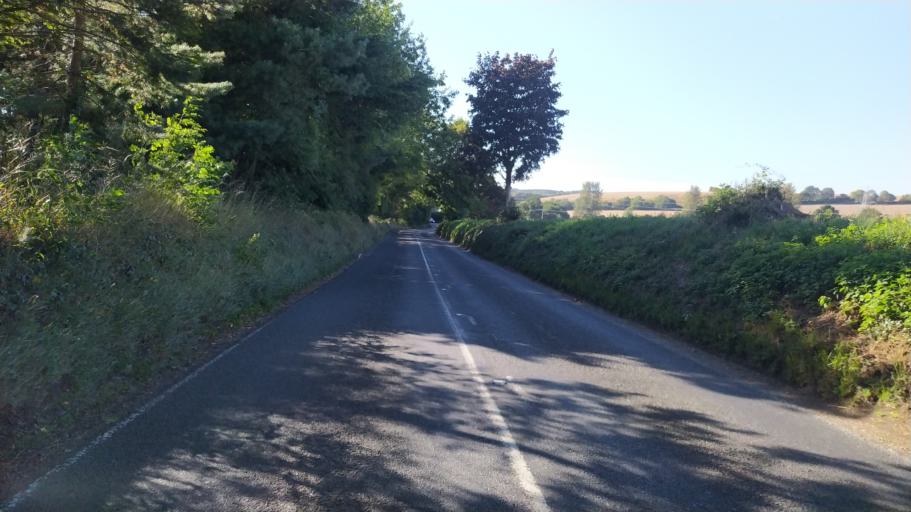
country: GB
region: England
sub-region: Hampshire
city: Alton
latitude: 51.1403
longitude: -0.9449
